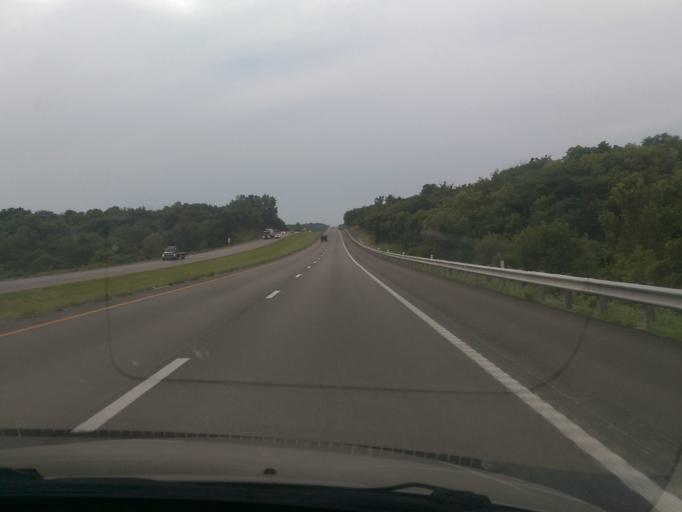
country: US
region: Missouri
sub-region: Andrew County
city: Savannah
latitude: 39.9275
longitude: -94.9194
